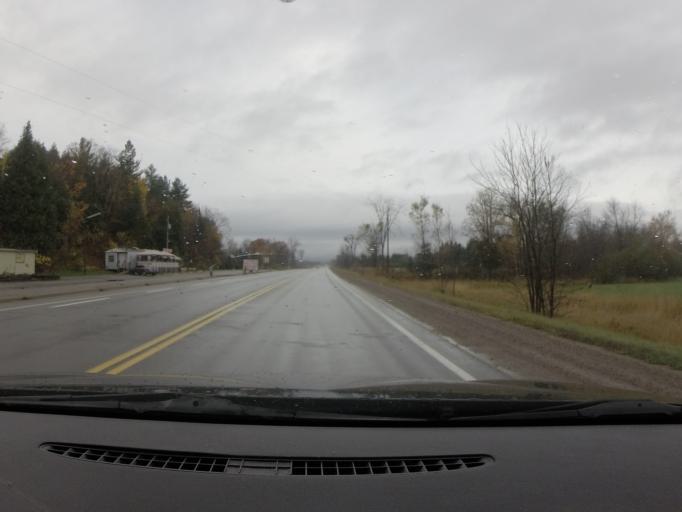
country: CA
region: Ontario
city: Belleville
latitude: 44.5583
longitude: -77.2570
